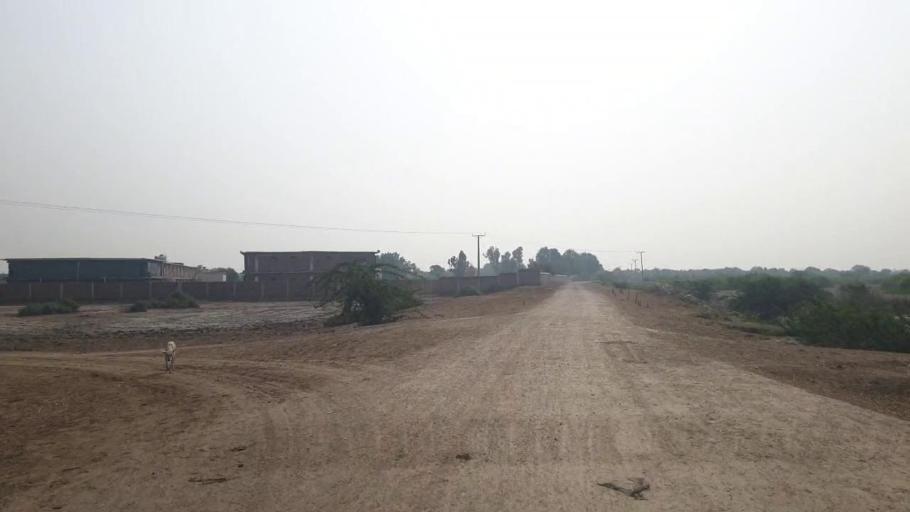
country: PK
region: Sindh
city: Tando Muhammad Khan
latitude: 25.2695
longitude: 68.5087
